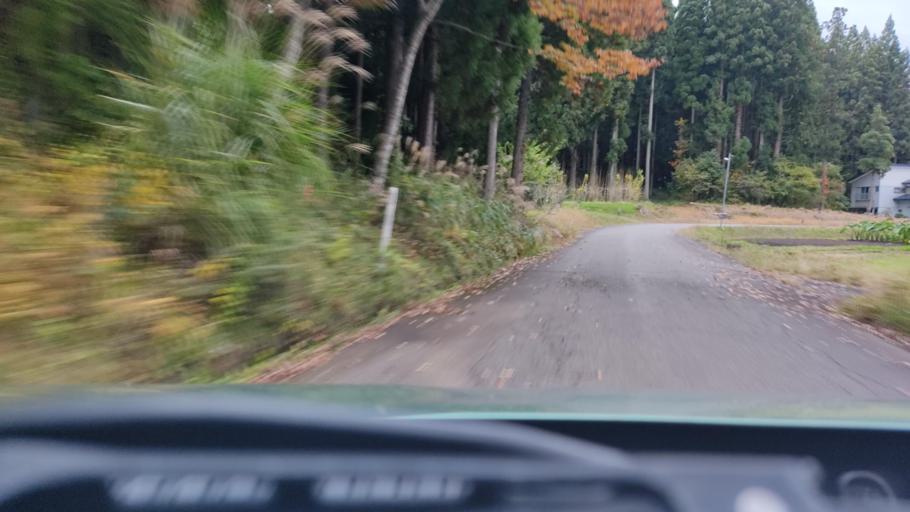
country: JP
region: Akita
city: Kakunodatemachi
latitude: 39.5482
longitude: 140.6233
